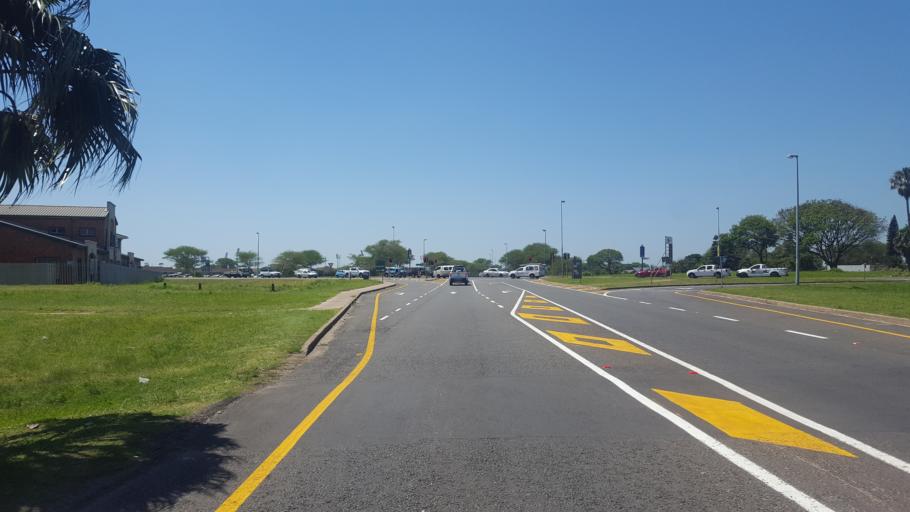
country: ZA
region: KwaZulu-Natal
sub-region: uThungulu District Municipality
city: Richards Bay
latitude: -28.7515
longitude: 32.0550
